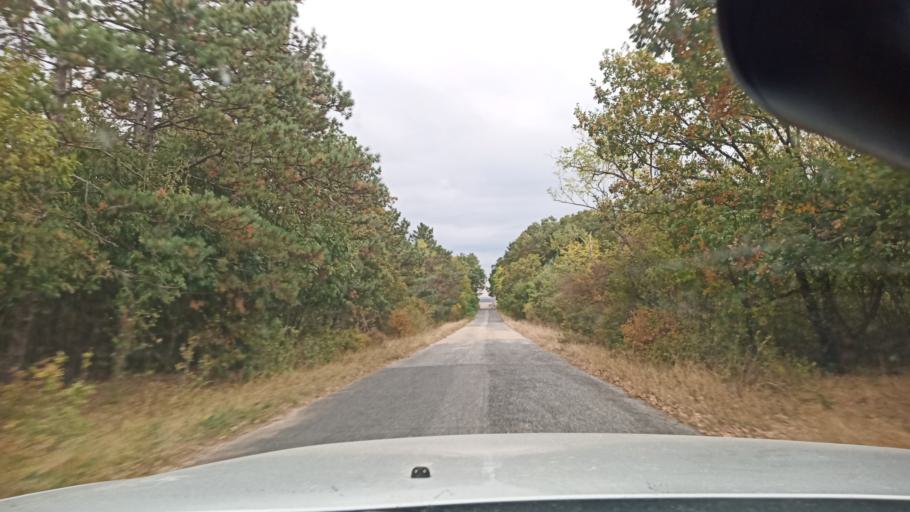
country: HU
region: Fejer
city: Zamoly
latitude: 47.3503
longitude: 18.3407
